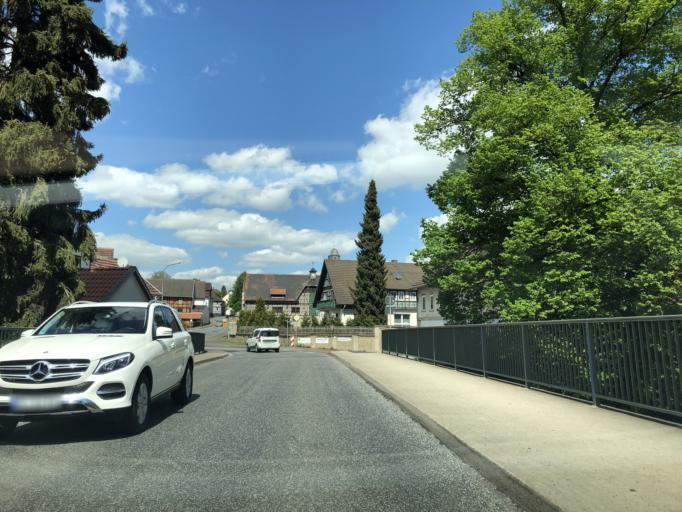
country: DE
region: Hesse
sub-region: Regierungsbezirk Kassel
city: Wabern
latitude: 51.1151
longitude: 9.3638
